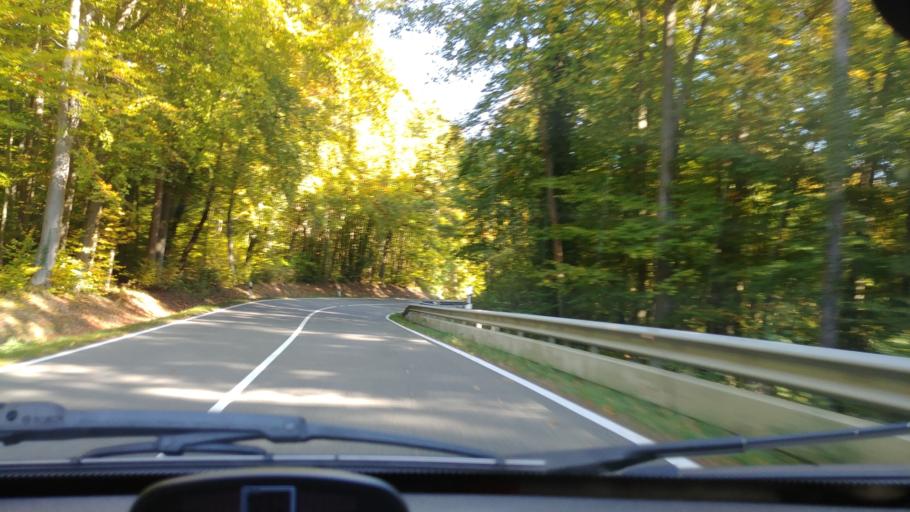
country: DE
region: Rheinland-Pfalz
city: Mudershausen
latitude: 50.2824
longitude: 8.0286
